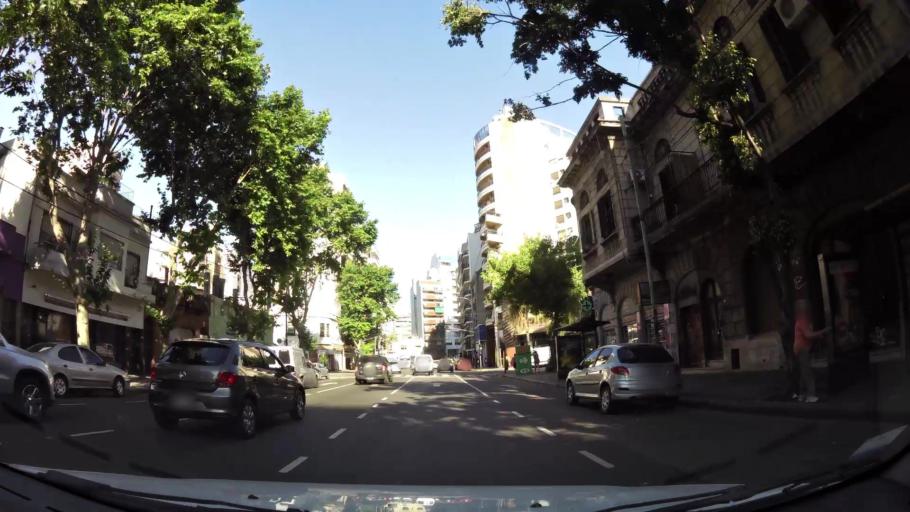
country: AR
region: Buenos Aires F.D.
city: Colegiales
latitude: -34.6082
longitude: -58.4430
